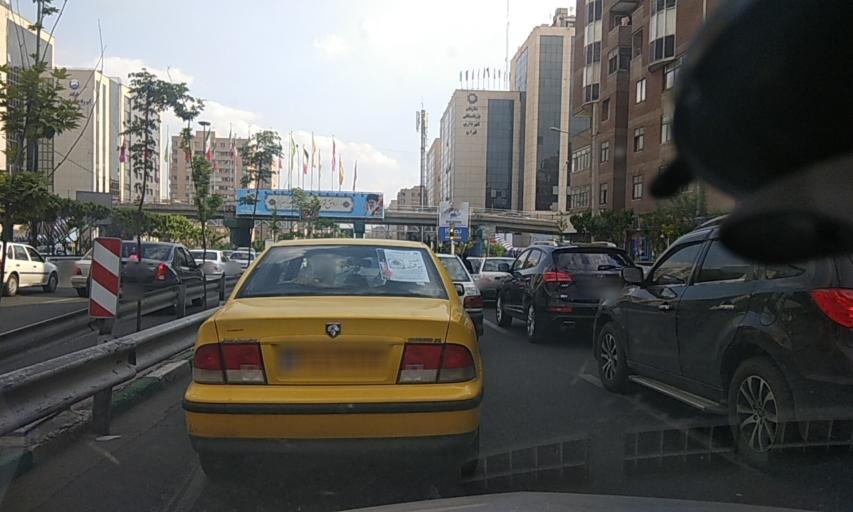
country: IR
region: Tehran
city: Tehran
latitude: 35.6892
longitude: 51.3791
